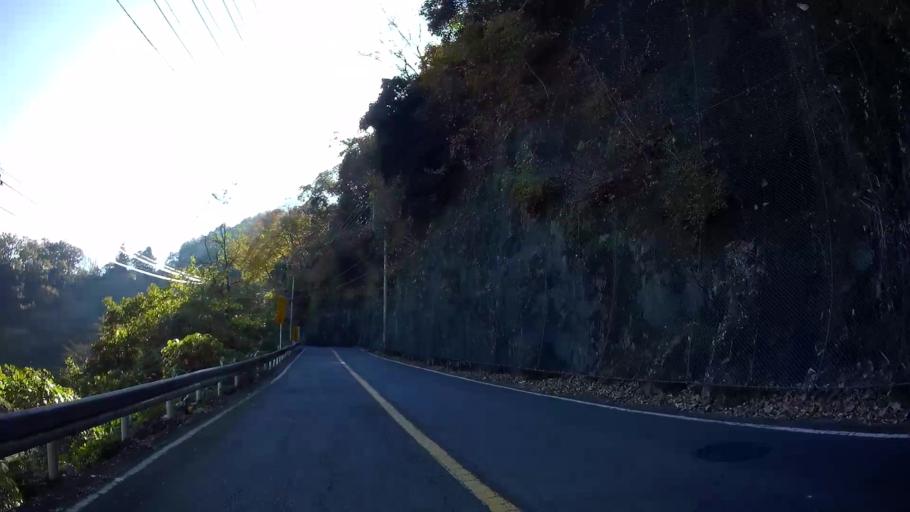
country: JP
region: Yamanashi
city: Uenohara
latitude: 35.6051
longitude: 139.1232
